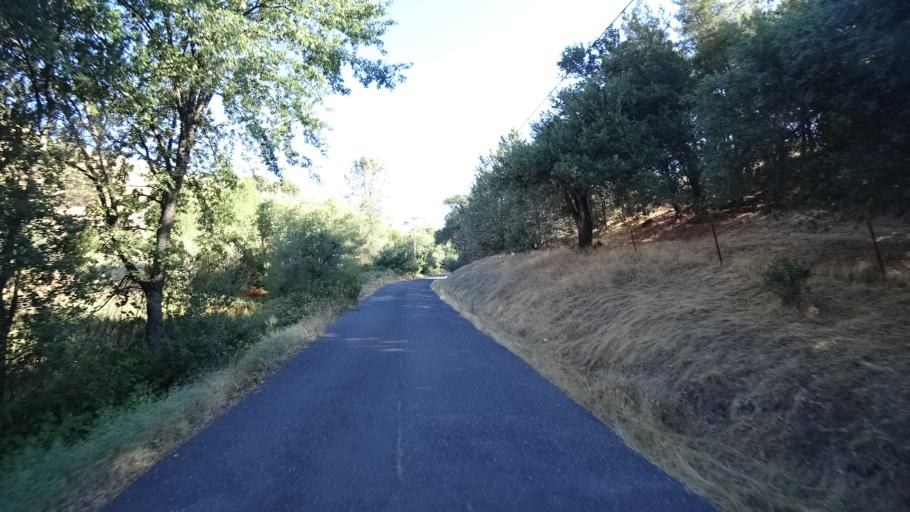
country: US
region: California
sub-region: Calaveras County
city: Angels Camp
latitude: 38.0535
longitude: -120.5071
